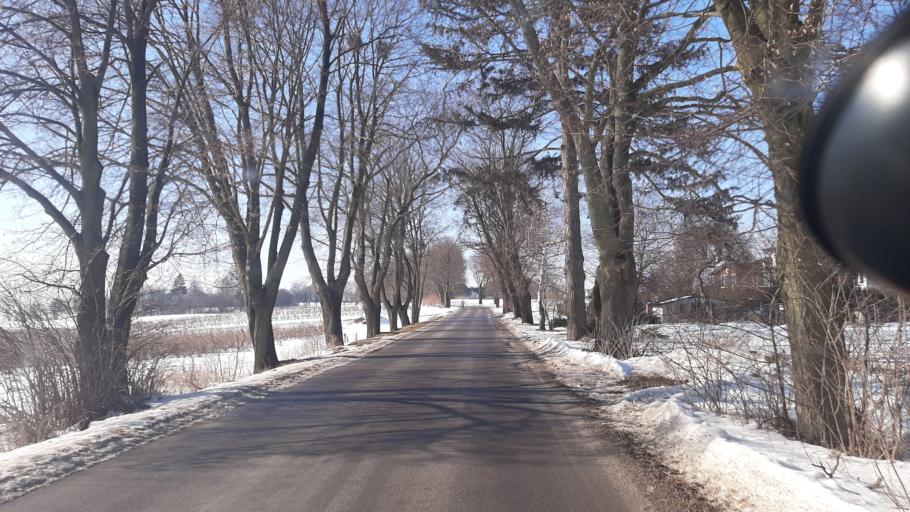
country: PL
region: Lublin Voivodeship
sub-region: Powiat pulawski
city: Naleczow
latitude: 51.3019
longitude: 22.2446
